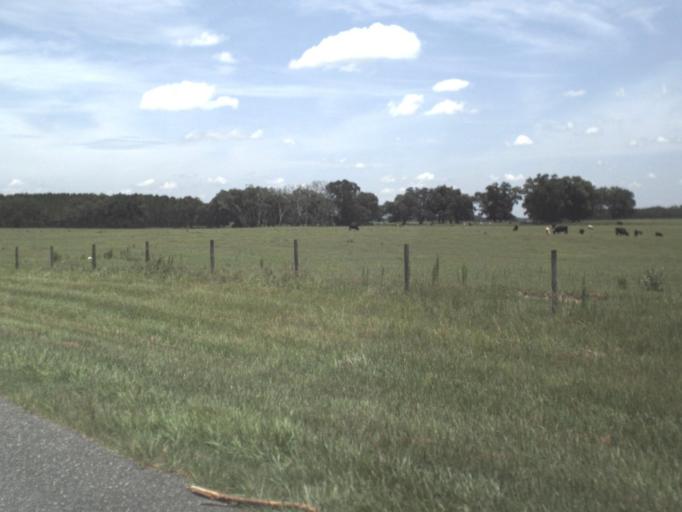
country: US
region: Florida
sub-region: Suwannee County
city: Live Oak
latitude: 30.2076
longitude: -83.0945
